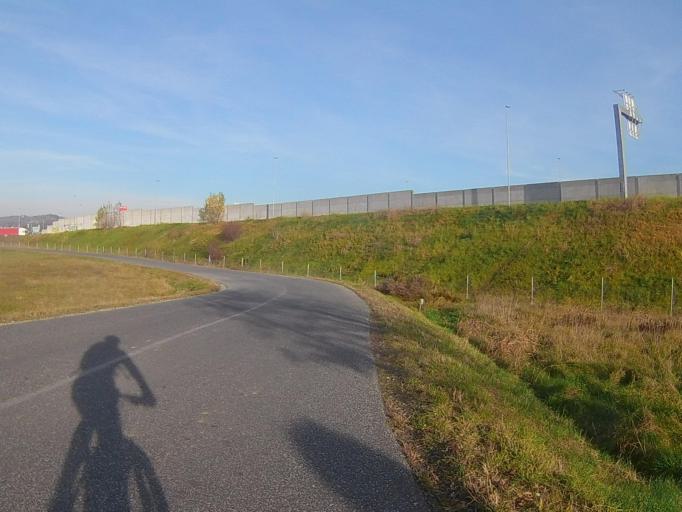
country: SI
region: Miklavz na Dravskem Polju
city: Miklavz na Dravskem Polju
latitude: 46.5288
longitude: 15.6978
